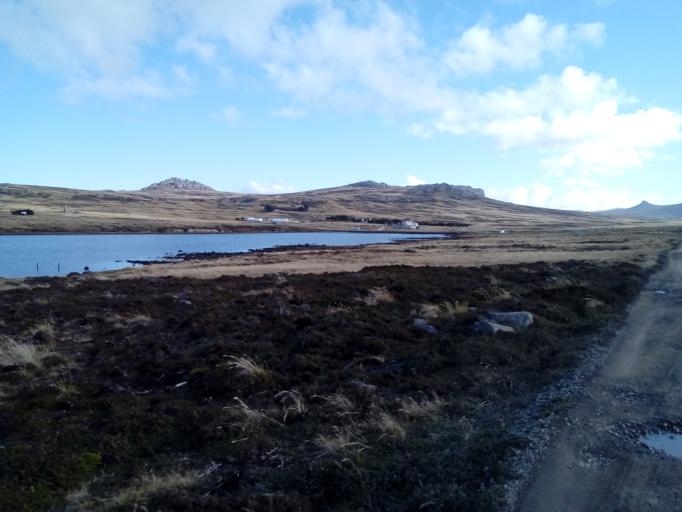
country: FK
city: Stanley
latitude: -51.6844
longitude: -57.9143
